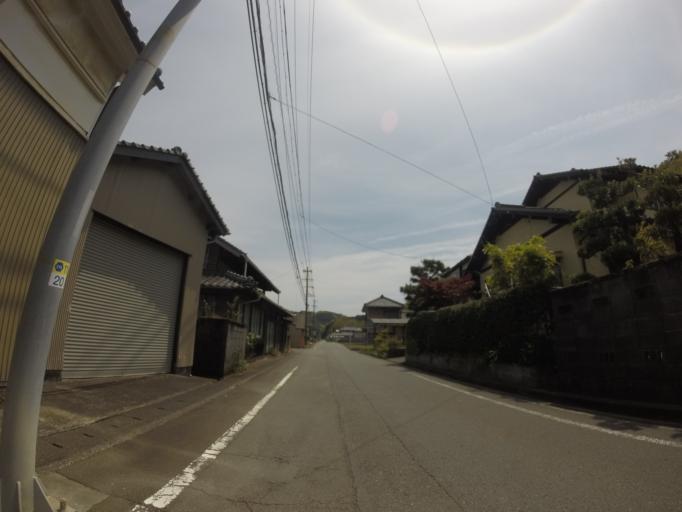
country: JP
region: Shizuoka
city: Fujieda
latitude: 34.9207
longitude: 138.2369
